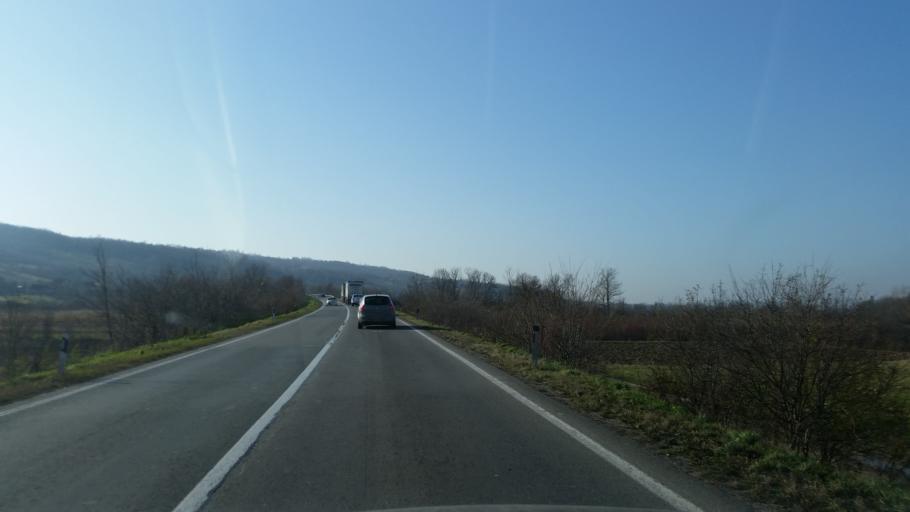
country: RS
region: Central Serbia
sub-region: Belgrade
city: Lazarevac
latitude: 44.3745
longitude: 20.2190
